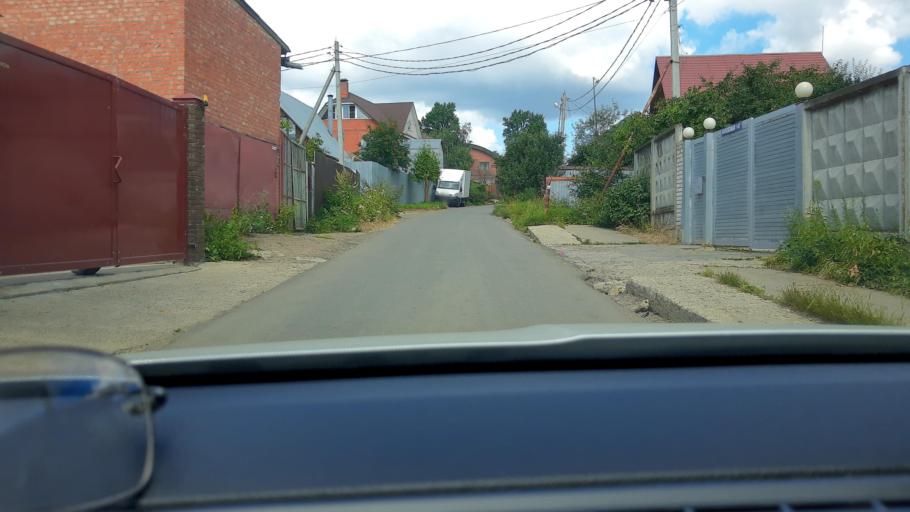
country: RU
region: Moskovskaya
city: Odintsovo
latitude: 55.6858
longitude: 37.3141
